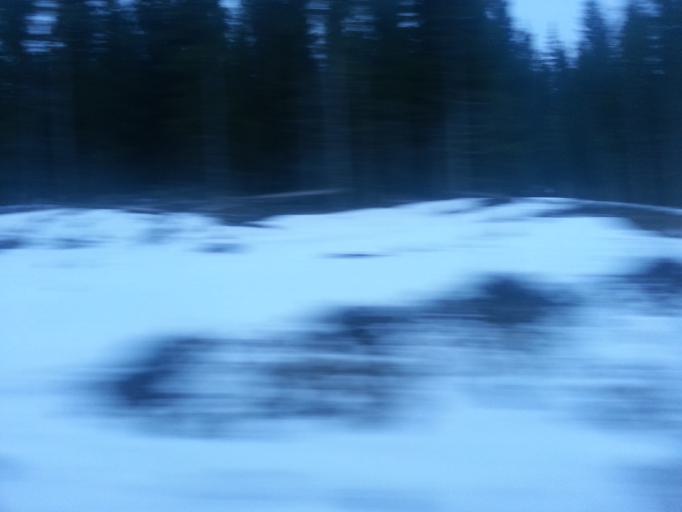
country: NO
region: Sor-Trondelag
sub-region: Rennebu
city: Berkak
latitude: 62.7908
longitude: 10.0115
